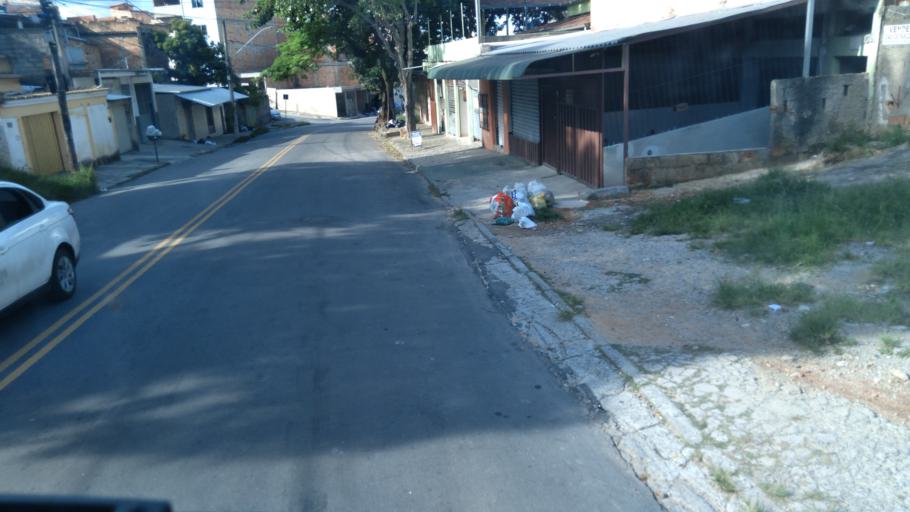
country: BR
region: Minas Gerais
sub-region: Belo Horizonte
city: Belo Horizonte
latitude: -19.8511
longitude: -43.9081
